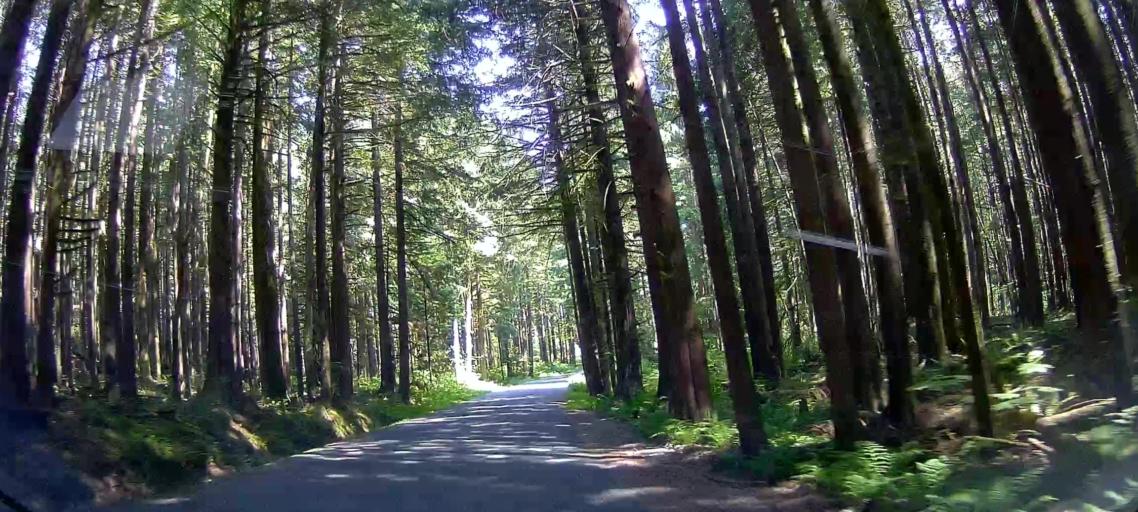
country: US
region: Washington
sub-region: Snohomish County
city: Arlington Heights
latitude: 48.3377
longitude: -122.0274
